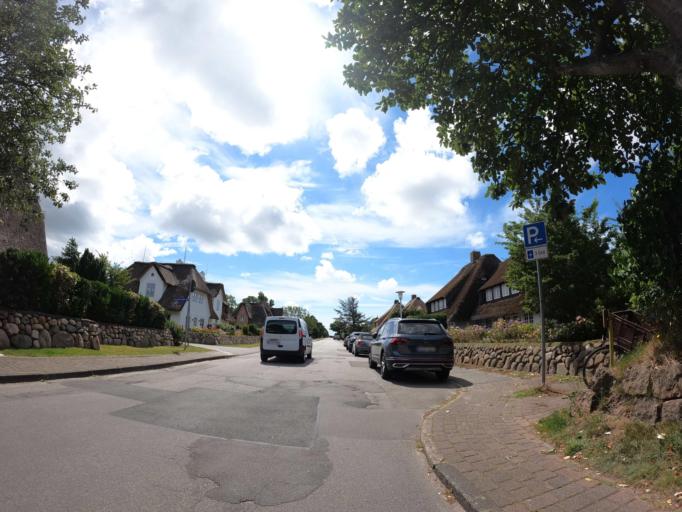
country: DE
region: Schleswig-Holstein
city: Keitum
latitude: 54.8949
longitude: 8.3648
